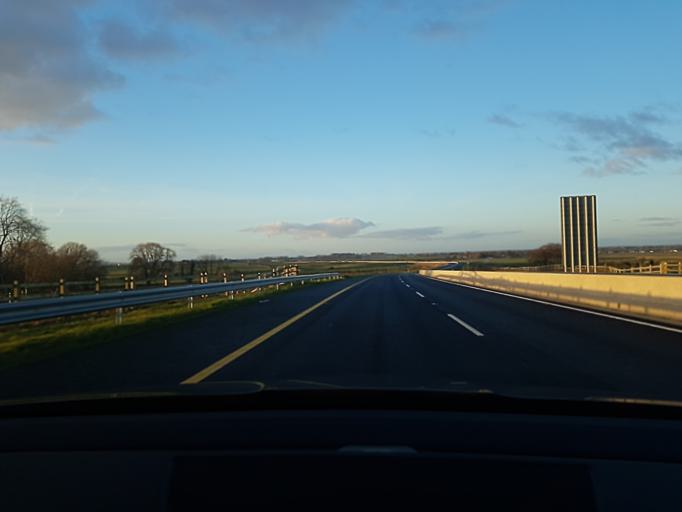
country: IE
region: Connaught
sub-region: County Galway
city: Tuam
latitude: 53.4148
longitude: -8.8289
